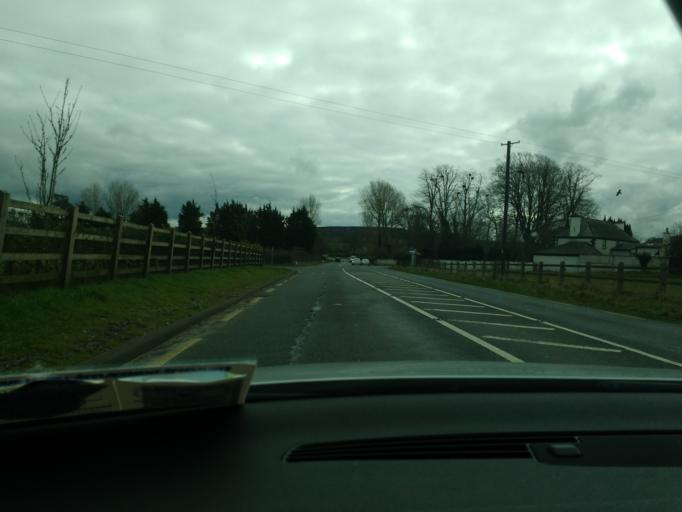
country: IE
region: Leinster
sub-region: Kilkenny
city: Ballyragget
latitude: 52.7124
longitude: -7.3278
